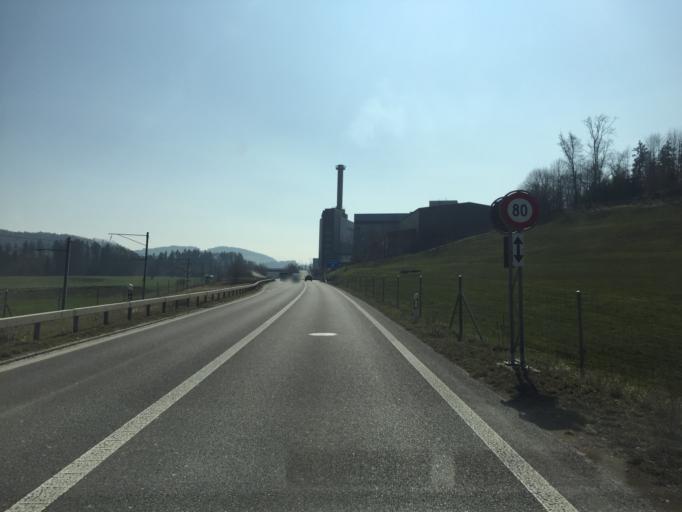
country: CH
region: Saint Gallen
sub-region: Wahlkreis Wil
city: Jonschwil
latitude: 47.4259
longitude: 9.0668
